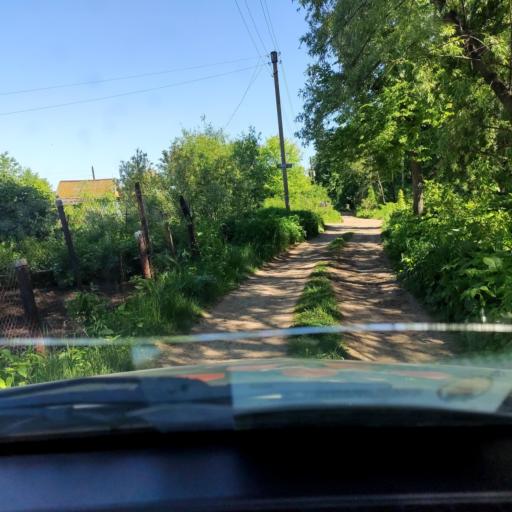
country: RU
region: Bashkortostan
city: Blagoveshchensk
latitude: 54.9406
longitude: 56.0859
